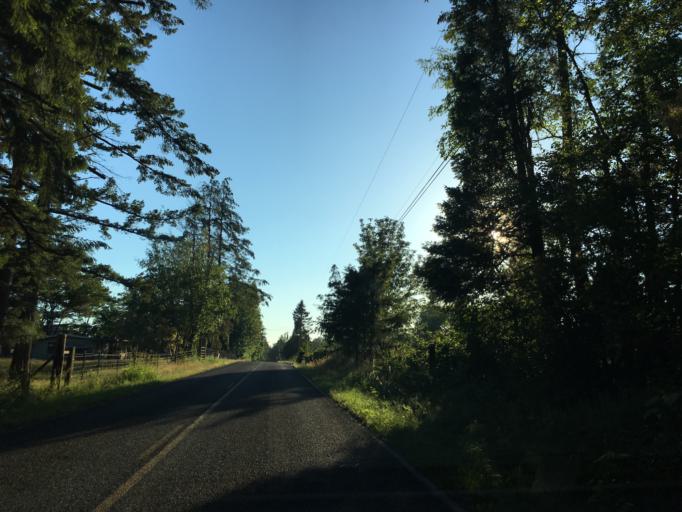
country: US
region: Washington
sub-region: Whatcom County
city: Geneva
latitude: 48.8186
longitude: -122.3875
